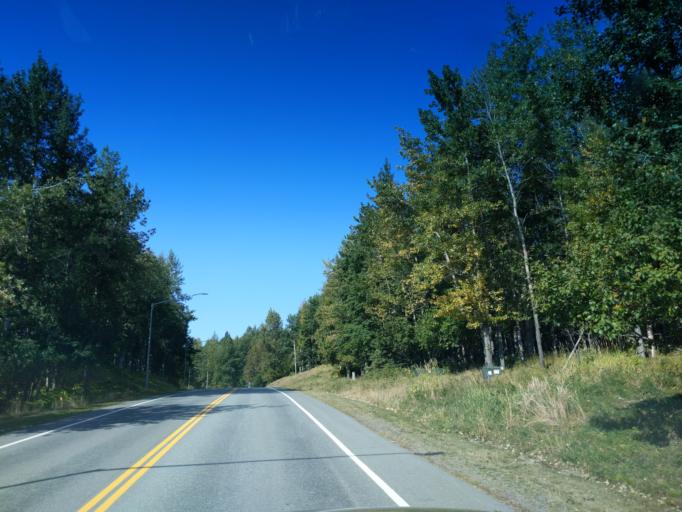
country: US
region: Alaska
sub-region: Anchorage Municipality
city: Anchorage
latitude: 61.1547
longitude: -150.0346
